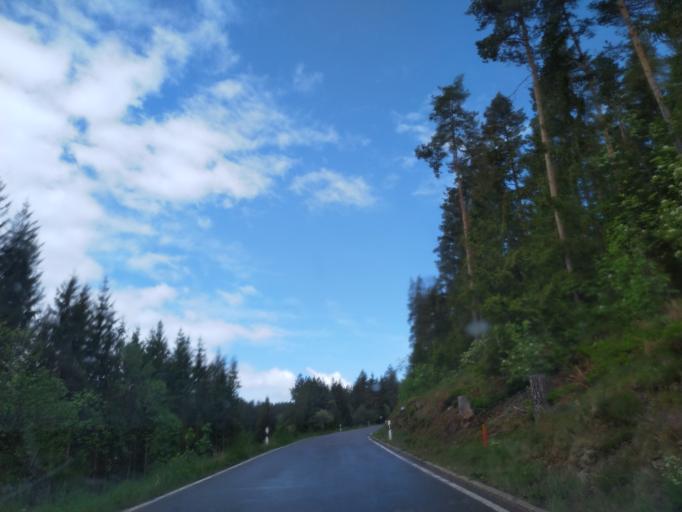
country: DE
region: Baden-Wuerttemberg
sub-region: Freiburg Region
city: Friedenweiler
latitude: 47.9339
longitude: 8.2549
